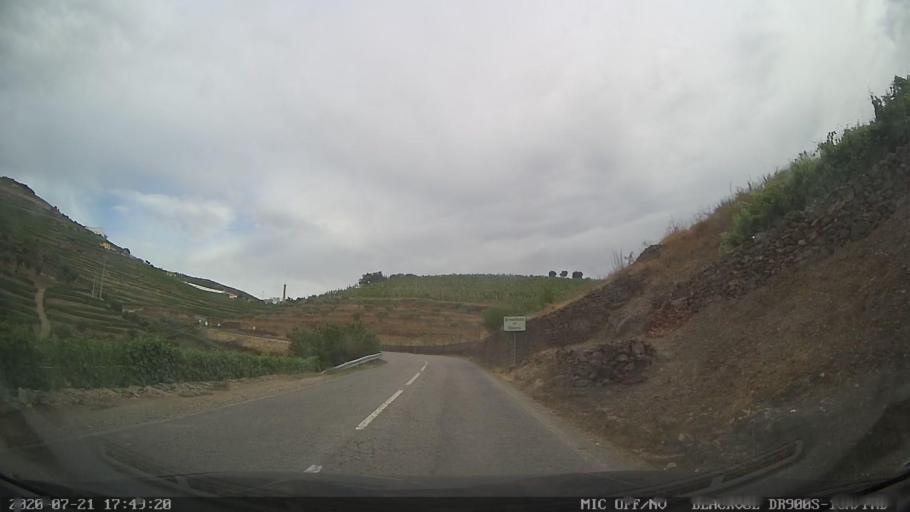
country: PT
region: Viseu
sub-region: Sao Joao da Pesqueira
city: Sao Joao da Pesqueira
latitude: 41.1720
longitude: -7.4803
